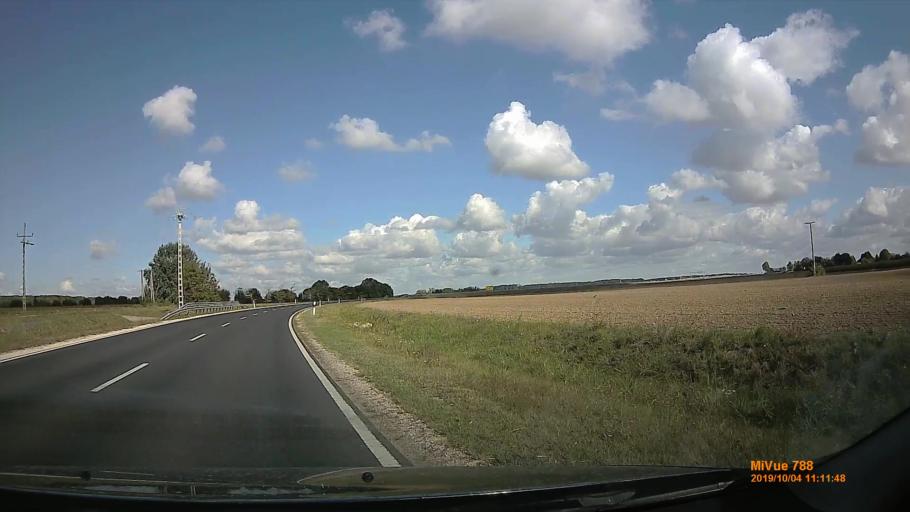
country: HU
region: Somogy
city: Kaposvar
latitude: 46.4184
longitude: 17.7683
